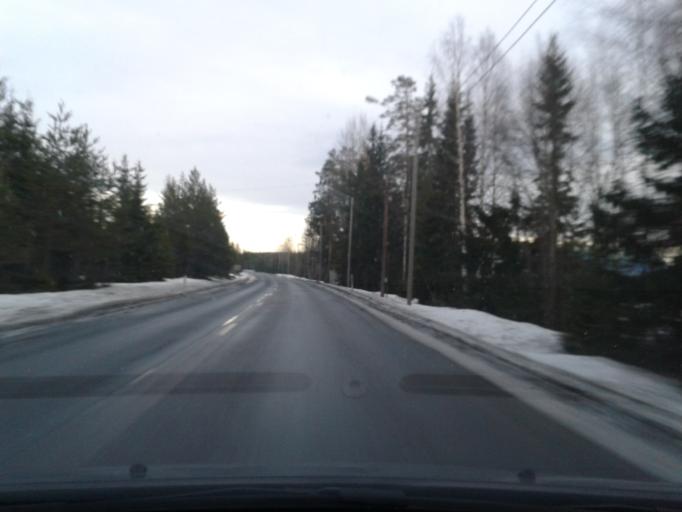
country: SE
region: Vaesternorrland
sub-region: Solleftea Kommun
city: Solleftea
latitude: 63.1525
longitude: 17.3326
